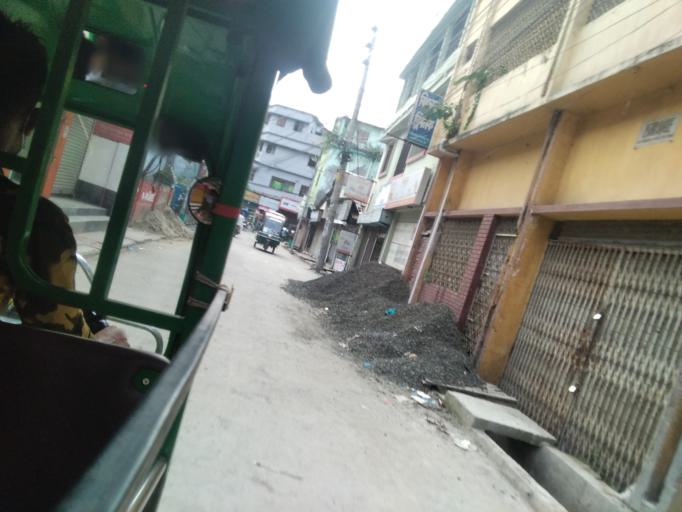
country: BD
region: Khulna
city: Khulna
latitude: 22.8156
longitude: 89.5629
